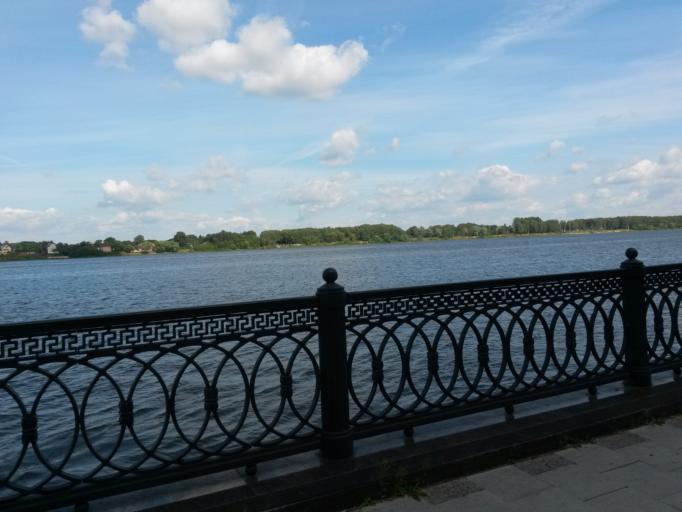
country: RU
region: Jaroslavl
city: Yaroslavl
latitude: 57.6289
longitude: 39.8979
